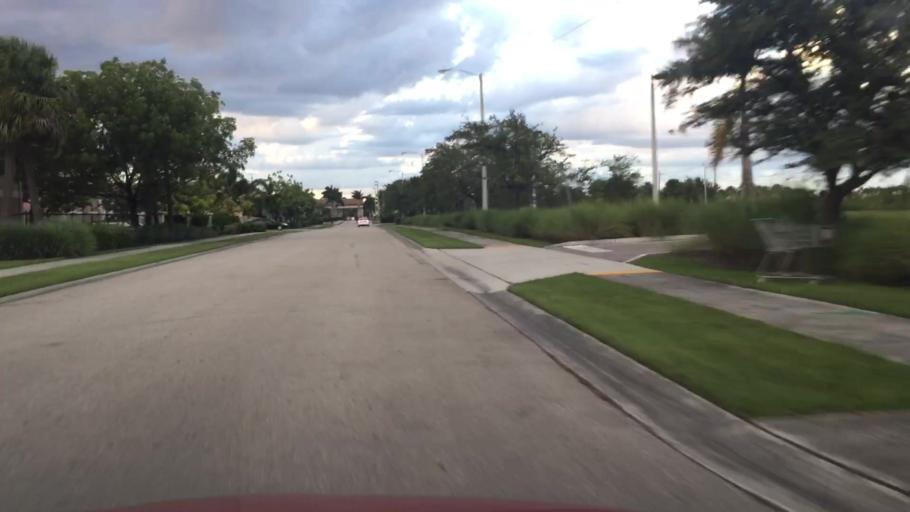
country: US
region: Florida
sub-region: Lee County
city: Fort Myers
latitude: 26.6000
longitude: -81.8122
